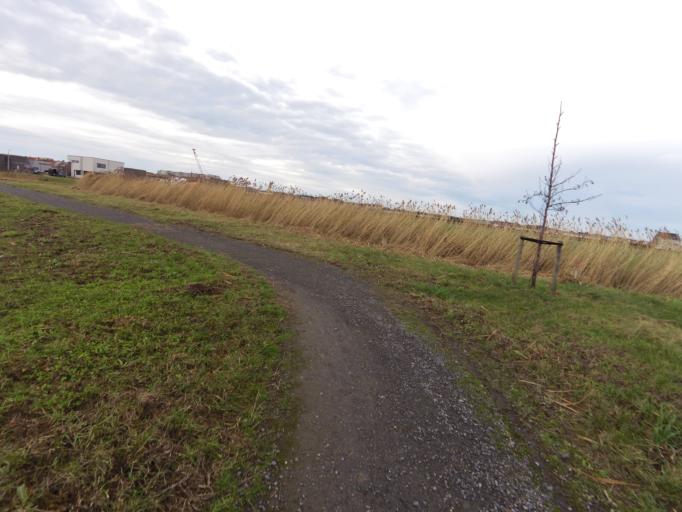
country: BE
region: Flanders
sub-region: Provincie West-Vlaanderen
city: Middelkerke
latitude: 51.1895
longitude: 2.8356
